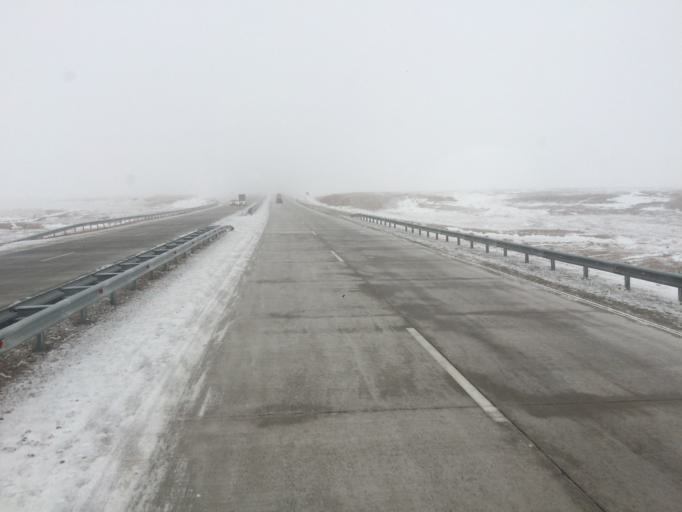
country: KZ
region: Zhambyl
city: Georgiyevka
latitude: 43.4139
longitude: 75.0441
